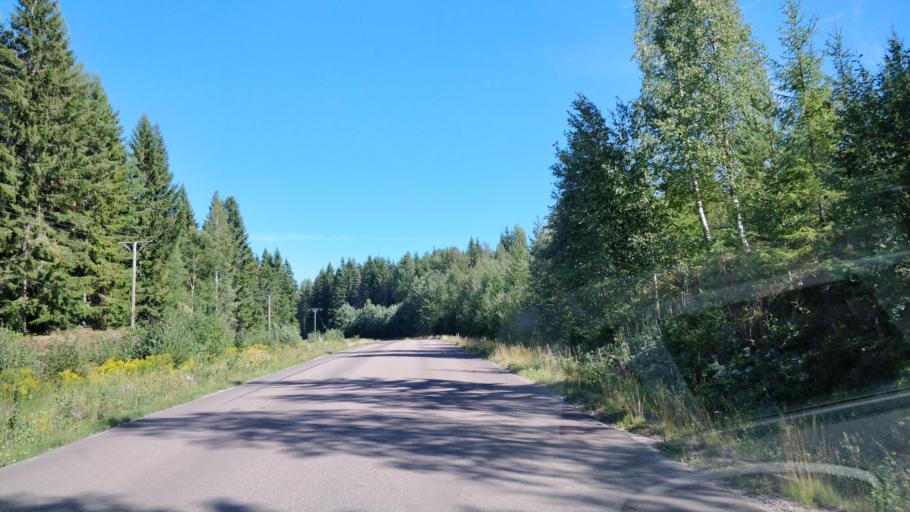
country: SE
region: Vaermland
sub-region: Hagfors Kommun
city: Hagfors
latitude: 60.0381
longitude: 13.7266
